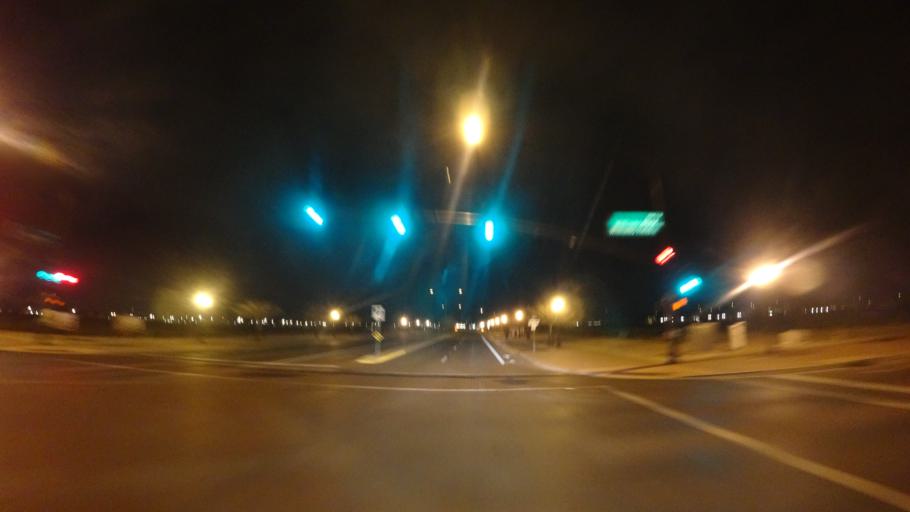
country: US
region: Arizona
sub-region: Maricopa County
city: Queen Creek
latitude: 33.3070
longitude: -111.7038
